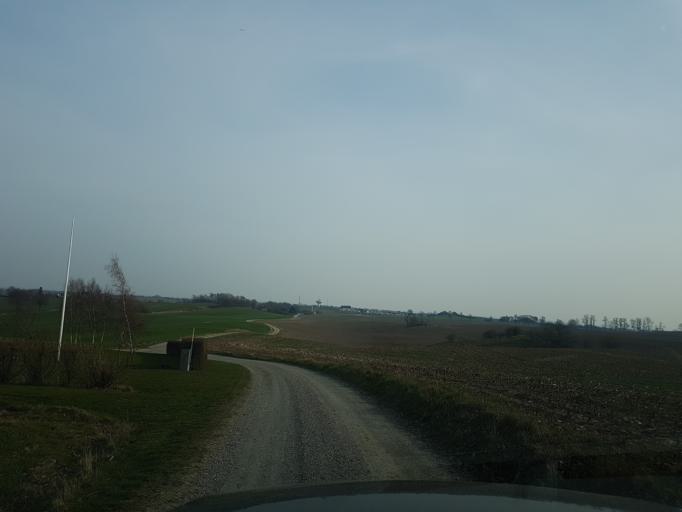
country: SE
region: Skane
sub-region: Ystads Kommun
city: Ystad
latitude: 55.4582
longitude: 13.7889
